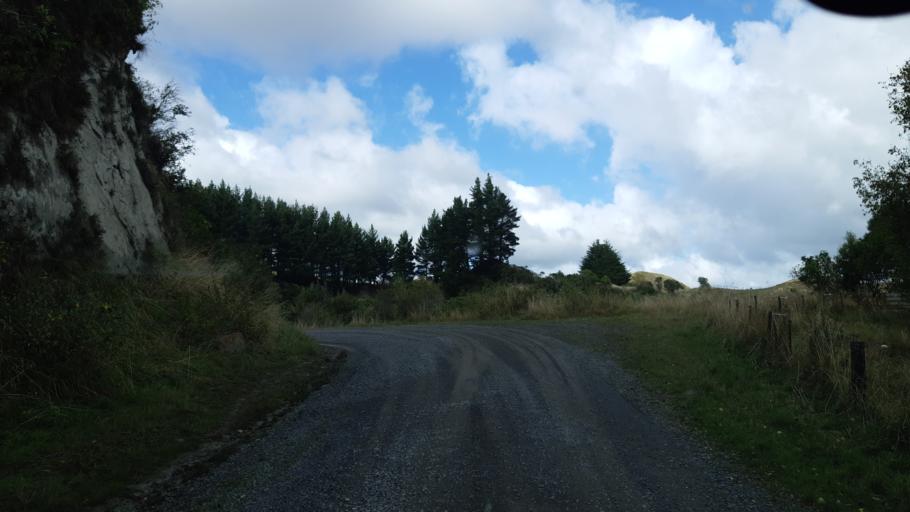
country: NZ
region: Manawatu-Wanganui
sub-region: Ruapehu District
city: Waiouru
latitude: -39.7803
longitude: 175.6809
